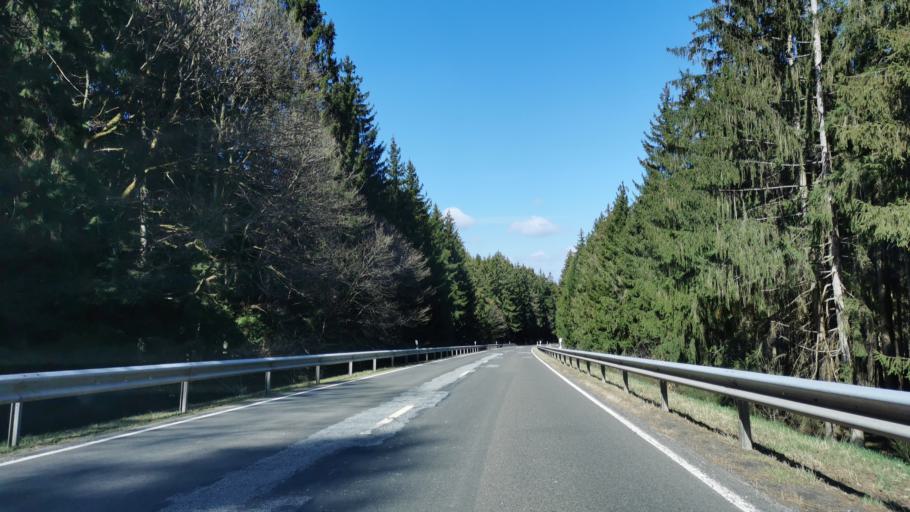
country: DE
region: Rheinland-Pfalz
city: Horath
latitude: 49.8292
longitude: 6.9904
